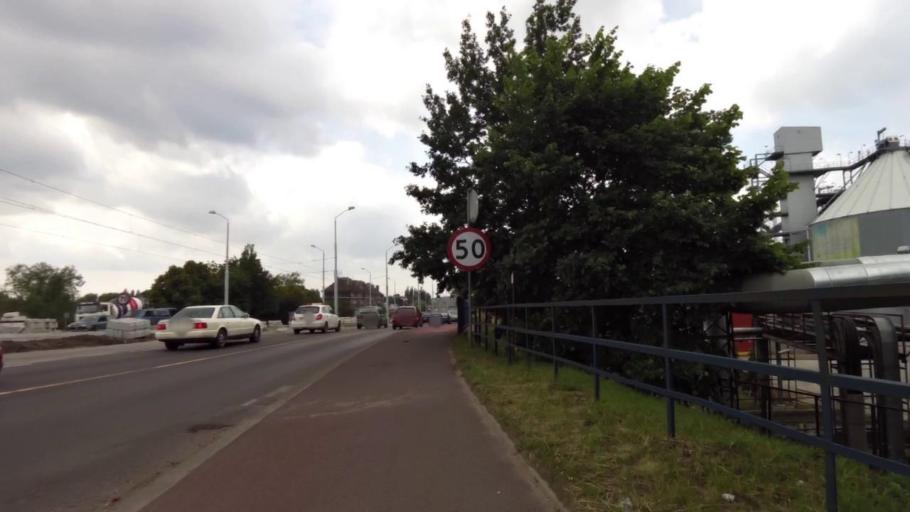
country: PL
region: West Pomeranian Voivodeship
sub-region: Szczecin
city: Szczecin
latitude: 53.4105
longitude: 14.5829
